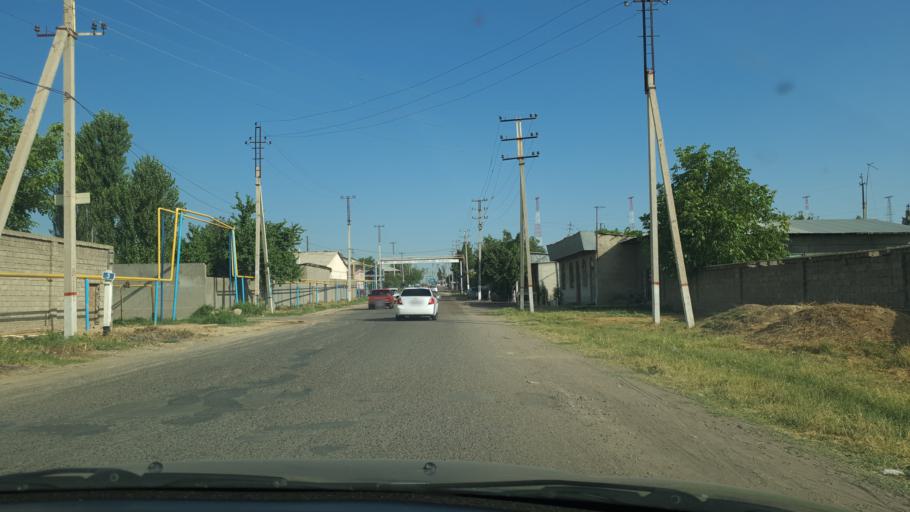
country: UZ
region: Toshkent
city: Urtaowul
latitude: 41.2052
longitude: 69.1506
